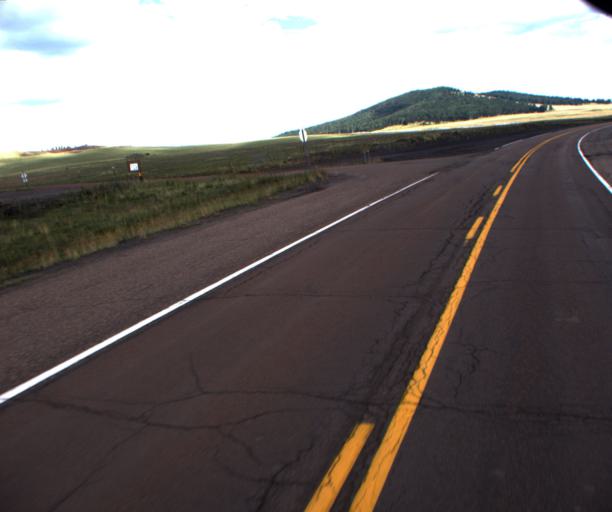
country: US
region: Arizona
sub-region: Apache County
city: Eagar
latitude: 34.0538
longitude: -109.5470
